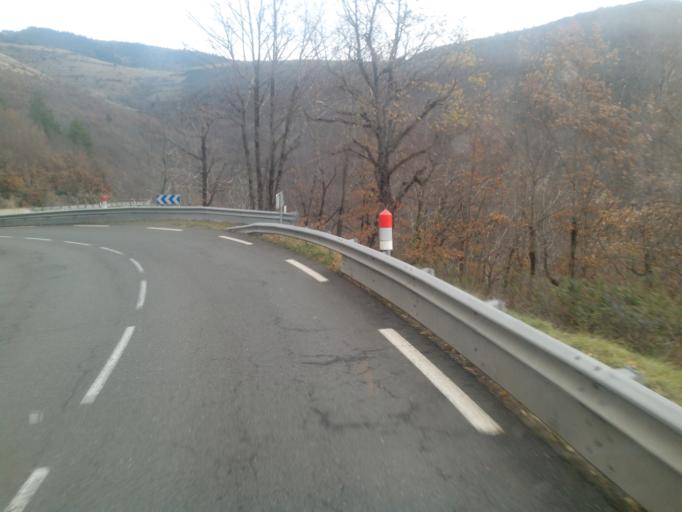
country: FR
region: Languedoc-Roussillon
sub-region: Departement de la Lozere
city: Florac
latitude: 44.3916
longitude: 3.5623
